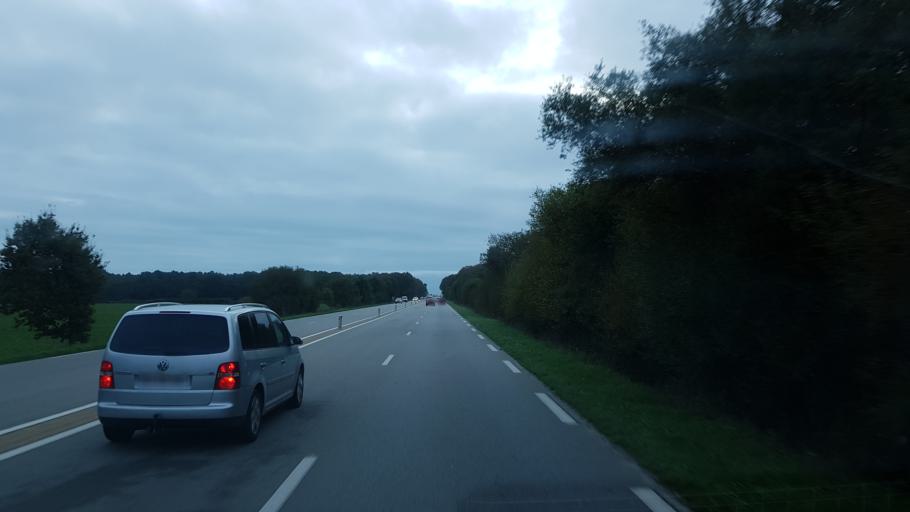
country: FR
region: Brittany
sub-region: Departement du Morbihan
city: Sarzeau
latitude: 47.5350
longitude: -2.7436
